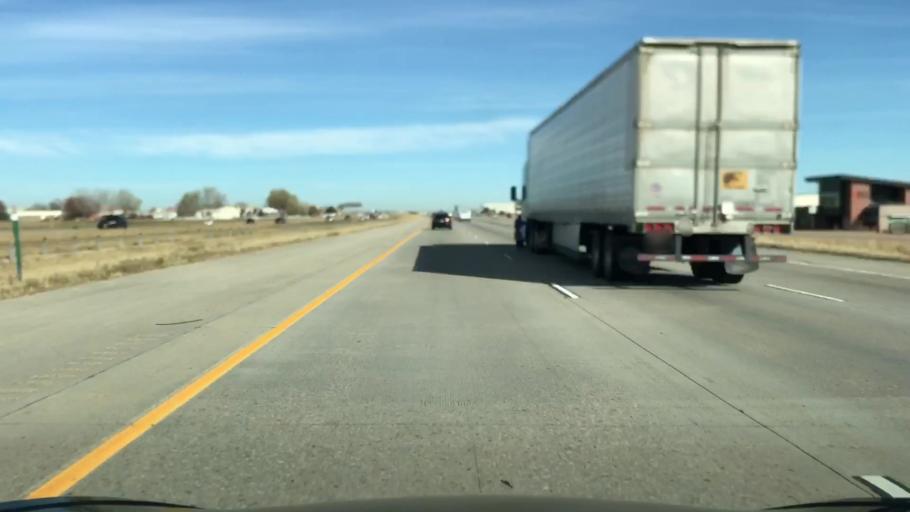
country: US
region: Colorado
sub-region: Weld County
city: Firestone
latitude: 40.1131
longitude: -104.9801
